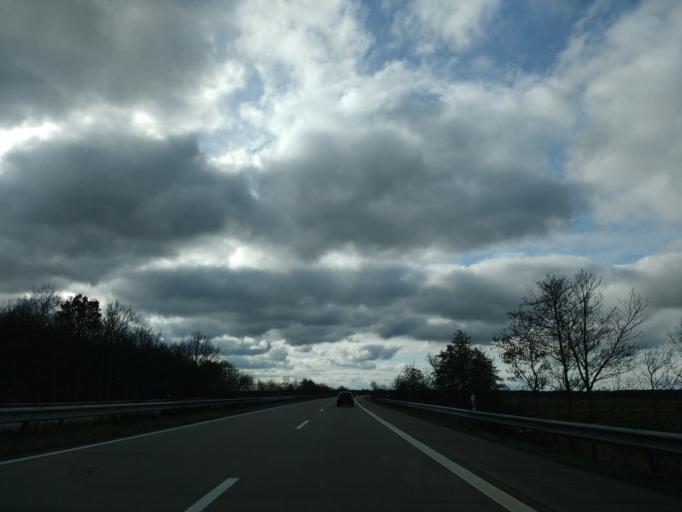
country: DE
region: Lower Saxony
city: Midlum
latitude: 53.7805
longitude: 8.7068
